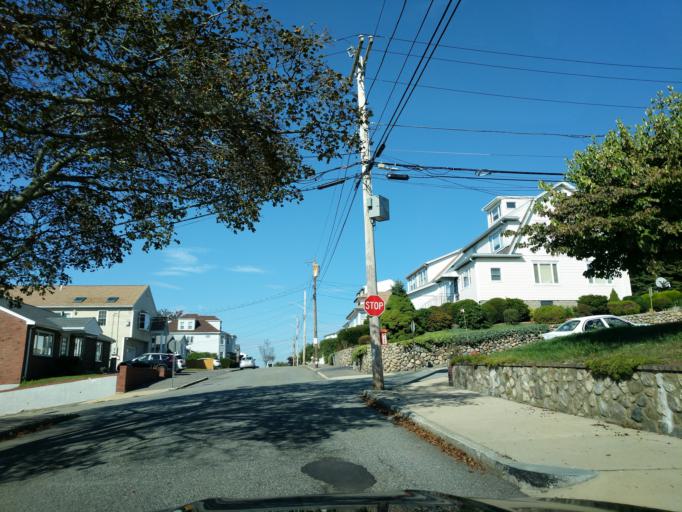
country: US
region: Massachusetts
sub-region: Suffolk County
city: Revere
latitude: 42.4080
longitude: -71.0204
